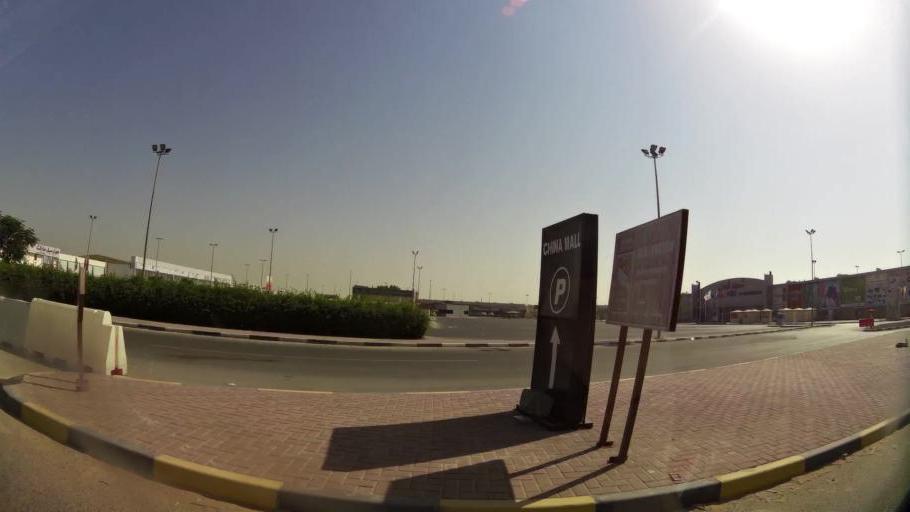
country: AE
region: Ajman
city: Ajman
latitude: 25.4280
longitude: 55.5217
